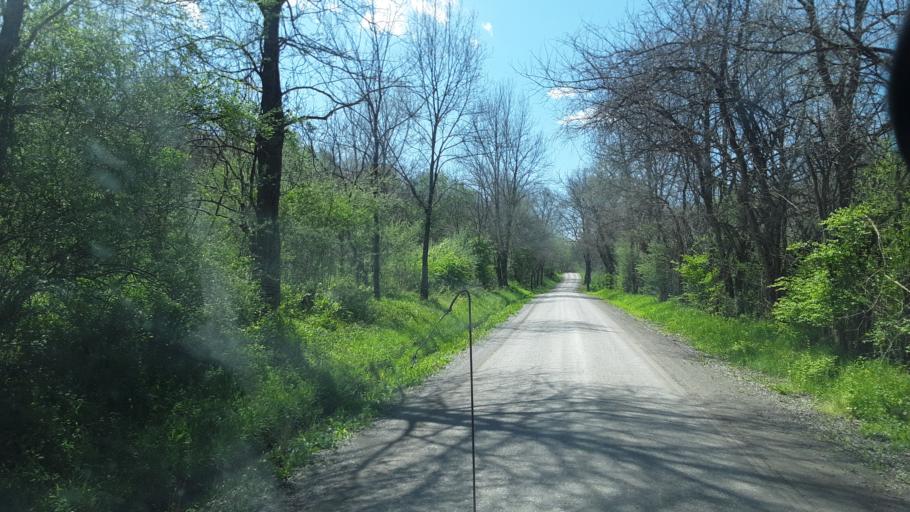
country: US
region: Ohio
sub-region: Noble County
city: Caldwell
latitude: 39.7600
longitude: -81.5877
